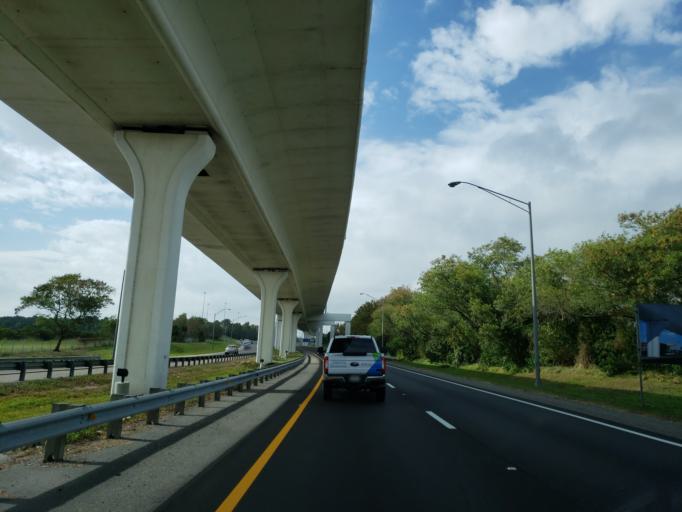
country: US
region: Florida
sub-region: Hillsborough County
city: Palm River-Clair Mel
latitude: 27.9480
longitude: -82.3683
